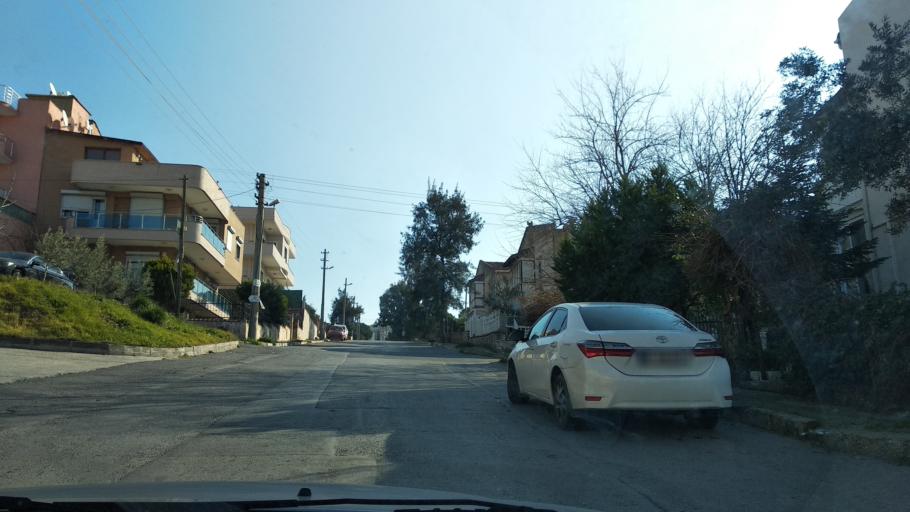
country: TR
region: Izmir
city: Karsiyaka
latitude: 38.4936
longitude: 27.0841
